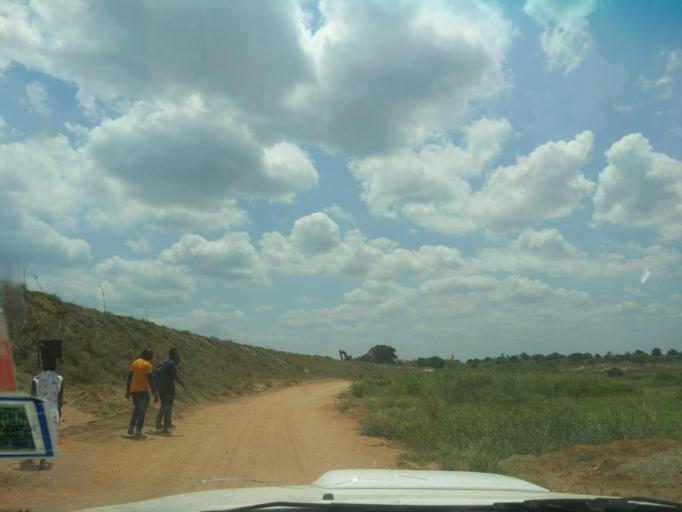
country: MZ
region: Zambezia
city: Quelimane
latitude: -17.2577
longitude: 37.0715
